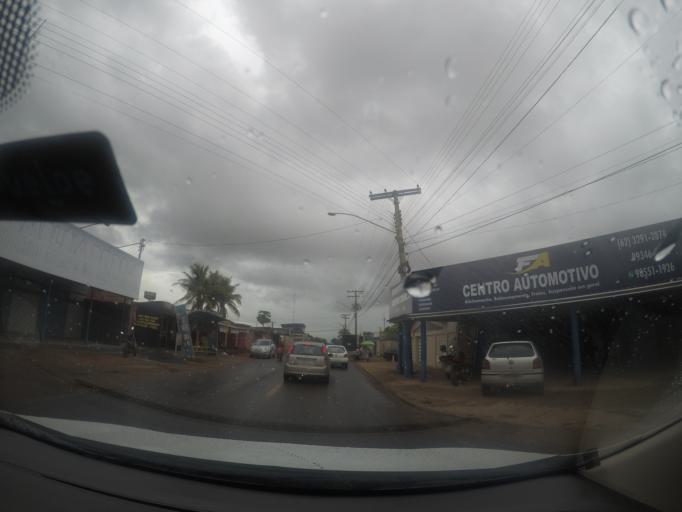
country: BR
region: Goias
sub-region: Trindade
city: Trindade
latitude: -16.6430
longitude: -49.4015
